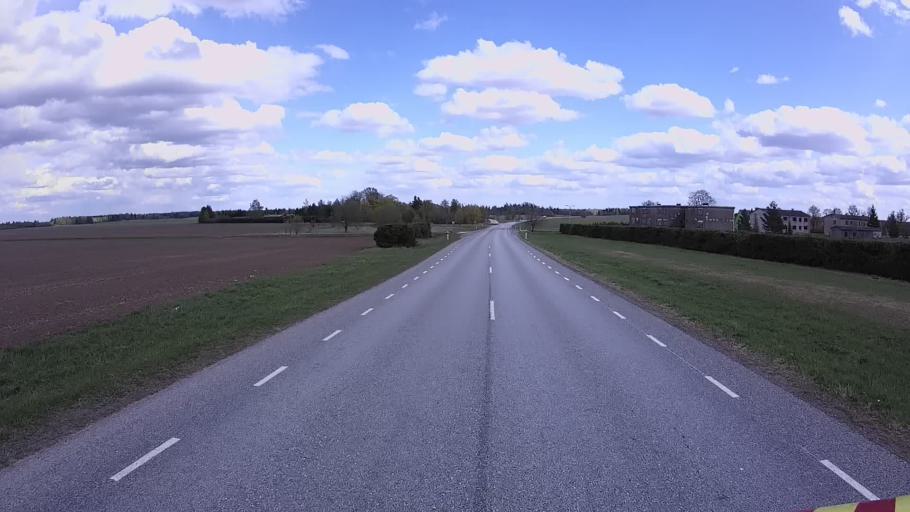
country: EE
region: Jaervamaa
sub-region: Koeru vald
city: Koeru
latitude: 58.9789
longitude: 26.0834
